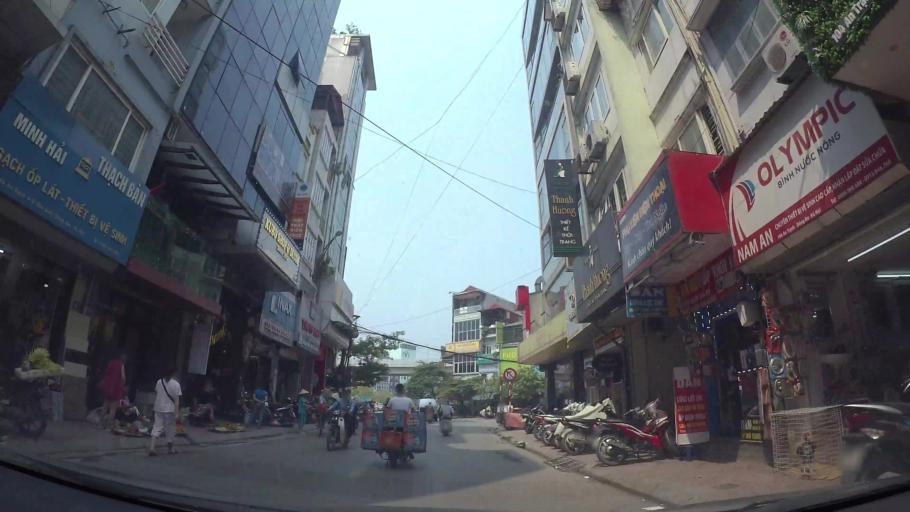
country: VN
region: Ha Noi
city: Dong Da
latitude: 21.0273
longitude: 105.8286
